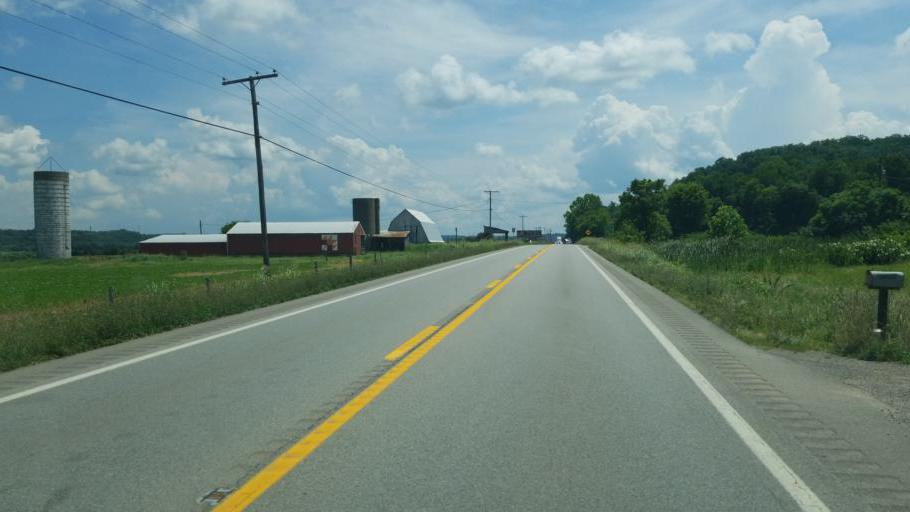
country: US
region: West Virginia
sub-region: Putnam County
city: Buffalo
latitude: 38.7588
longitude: -81.9946
